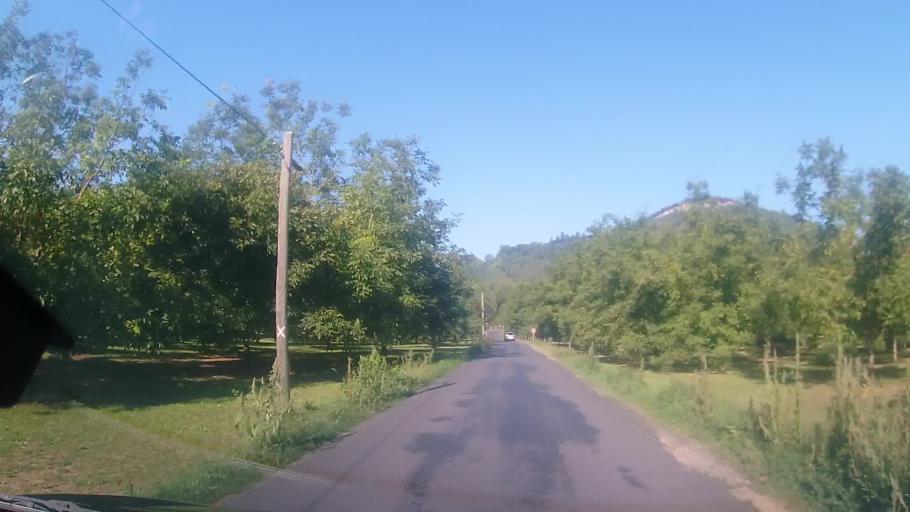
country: FR
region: Aquitaine
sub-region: Departement de la Dordogne
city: Cenac-et-Saint-Julien
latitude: 44.7953
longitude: 1.1650
